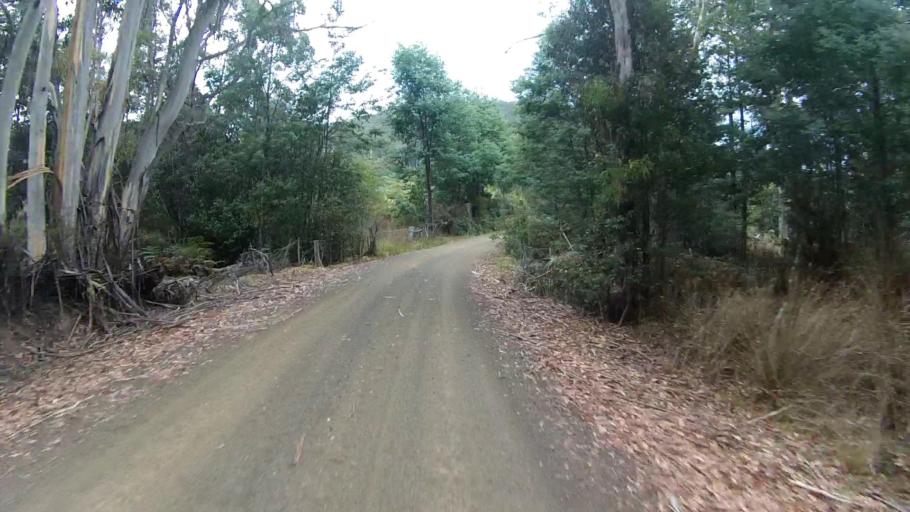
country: AU
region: Tasmania
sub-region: Kingborough
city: Kettering
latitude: -43.2213
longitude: 147.1762
